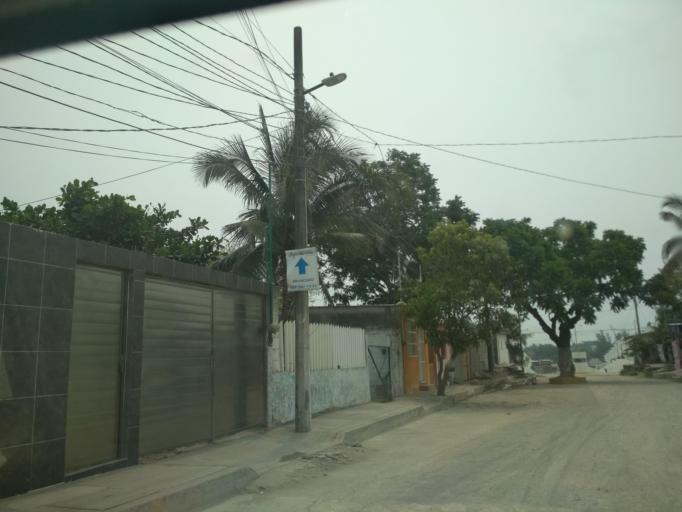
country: MX
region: Veracruz
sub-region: Veracruz
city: Colonia Chalchihuecan
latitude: 19.2113
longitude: -96.2139
